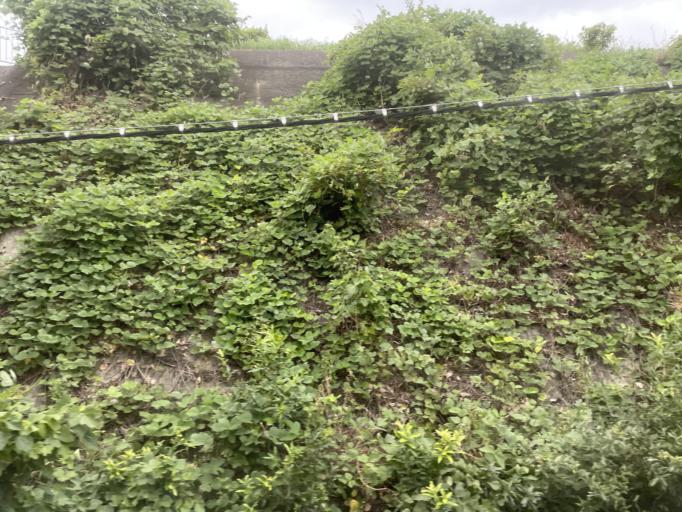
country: JP
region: Osaka
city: Kaizuka
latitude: 34.3658
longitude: 135.2875
